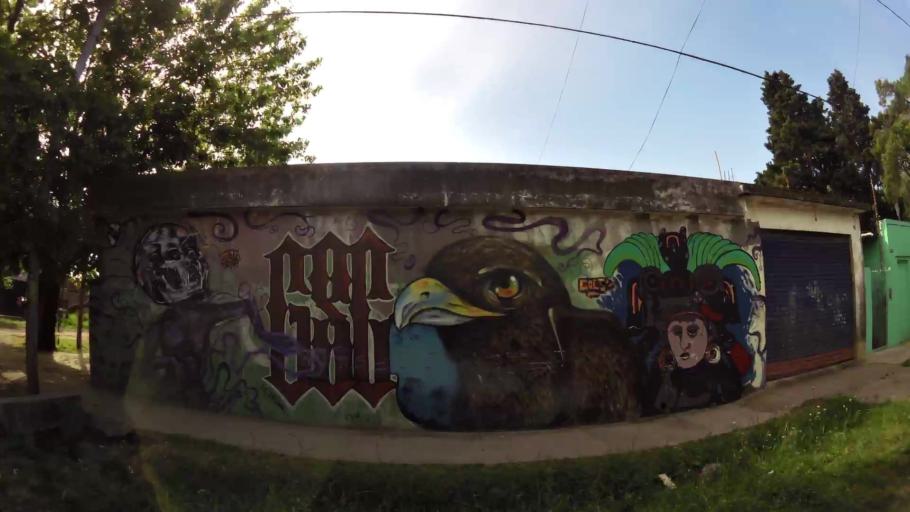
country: AR
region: Buenos Aires
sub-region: Partido de Almirante Brown
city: Adrogue
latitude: -34.8017
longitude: -58.3460
